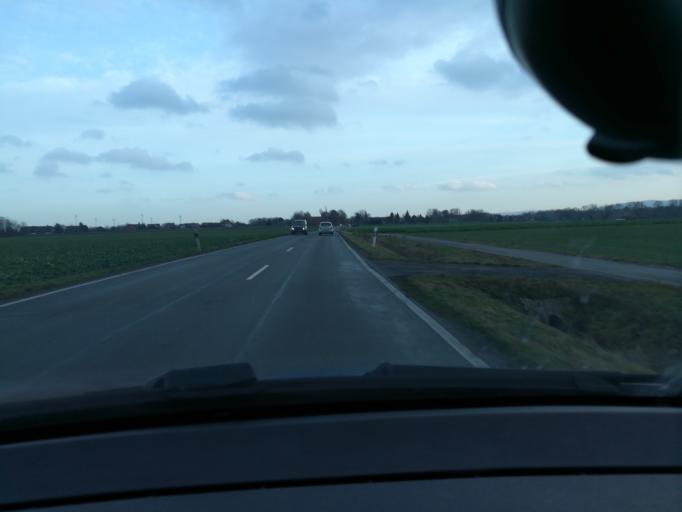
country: DE
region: North Rhine-Westphalia
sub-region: Regierungsbezirk Detmold
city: Hille
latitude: 52.3180
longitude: 8.8055
